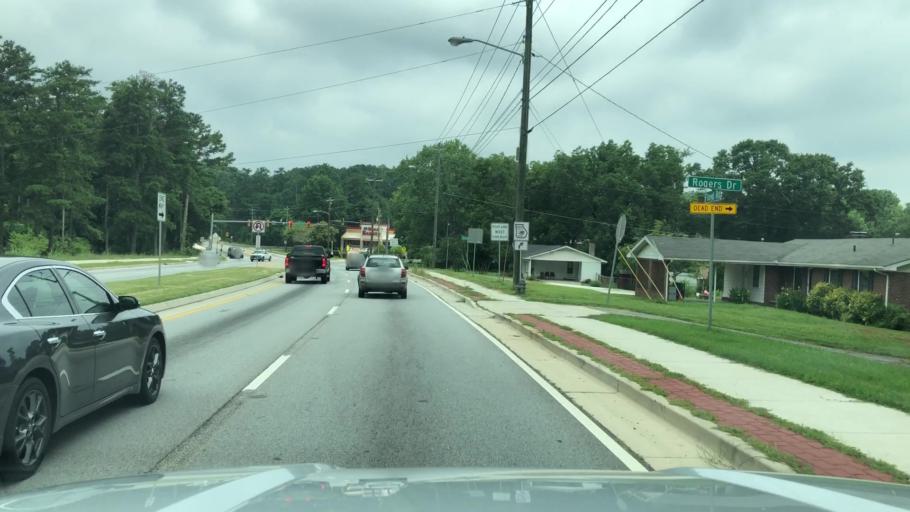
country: US
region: Georgia
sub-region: Cobb County
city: Mableton
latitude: 33.8394
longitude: -84.5772
